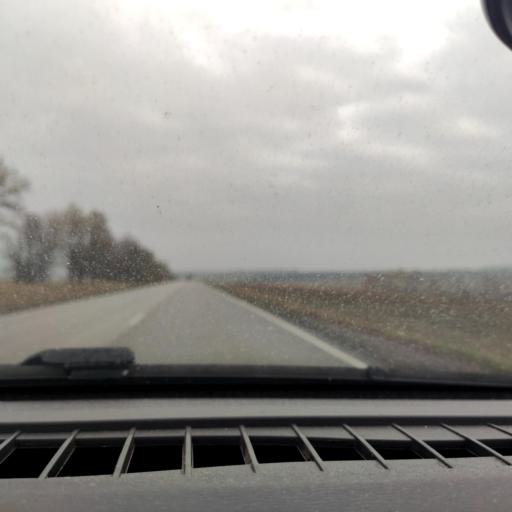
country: RU
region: Belgorod
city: Ilovka
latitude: 50.7623
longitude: 38.7411
